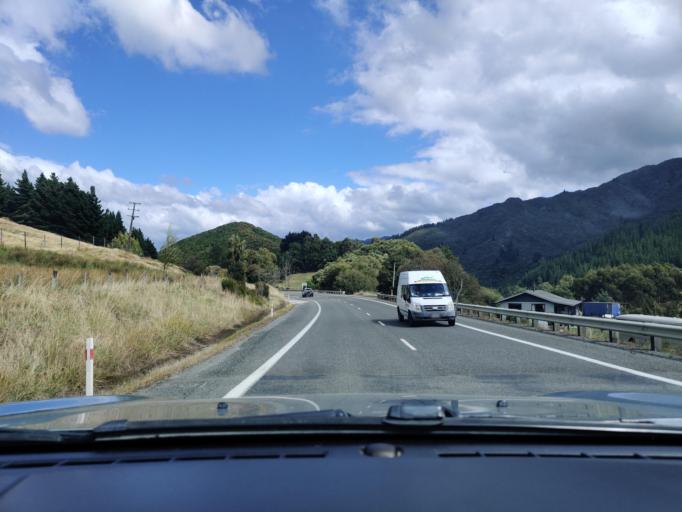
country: NZ
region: Marlborough
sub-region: Marlborough District
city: Picton
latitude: -41.3088
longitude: 173.9834
